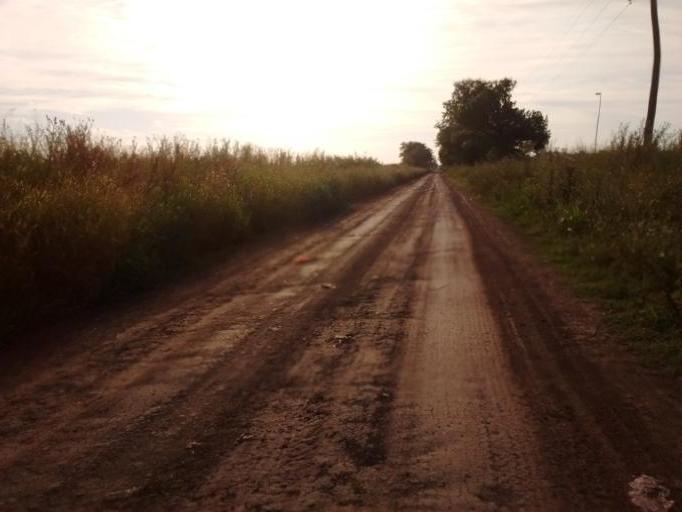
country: AR
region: Santa Fe
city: Funes
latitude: -32.9306
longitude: -60.8554
